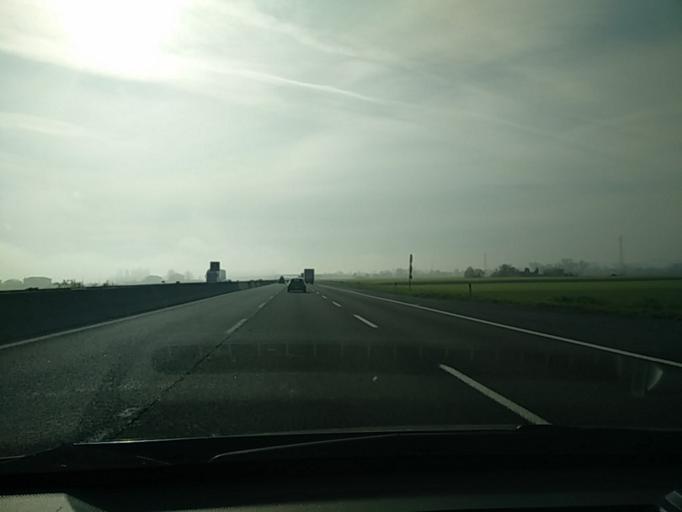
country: IT
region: Emilia-Romagna
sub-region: Provincia di Bologna
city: Osteria Grande
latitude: 44.4491
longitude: 11.5446
